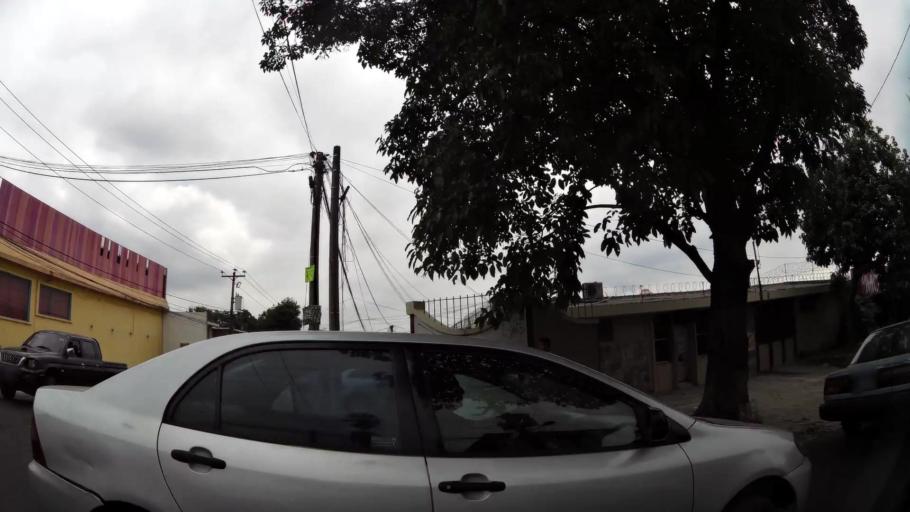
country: SV
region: La Libertad
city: Antiguo Cuscatlan
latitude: 13.7039
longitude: -89.2360
